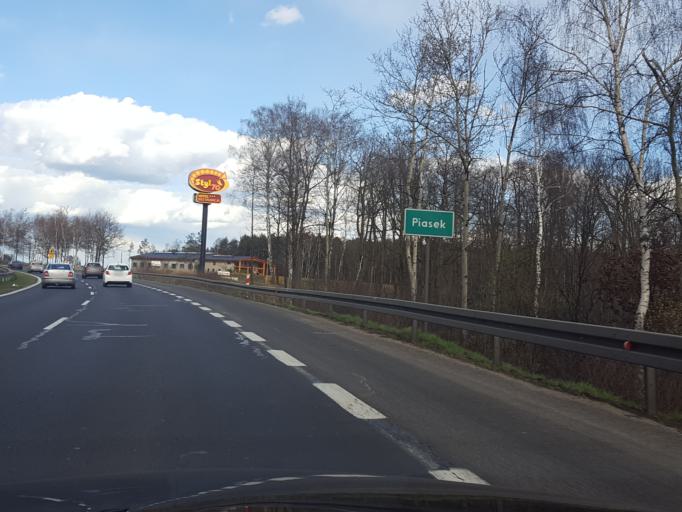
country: PL
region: Silesian Voivodeship
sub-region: Powiat pszczynski
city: Piasek
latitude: 50.0073
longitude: 18.9554
